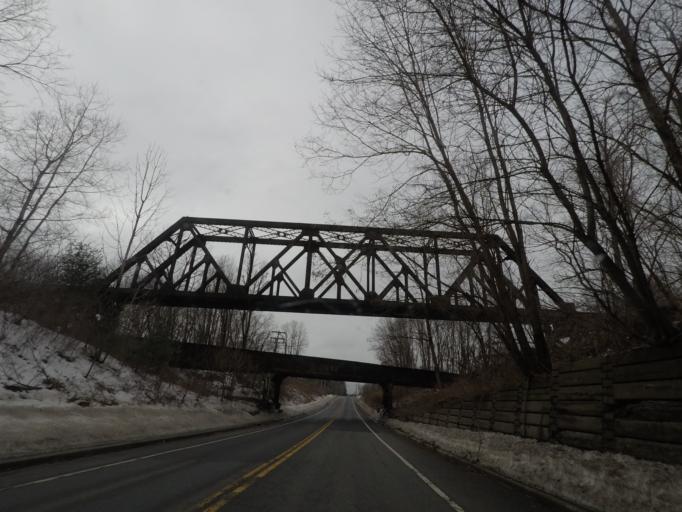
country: US
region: New York
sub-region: Schenectady County
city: Rotterdam
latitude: 42.7255
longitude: -73.9600
